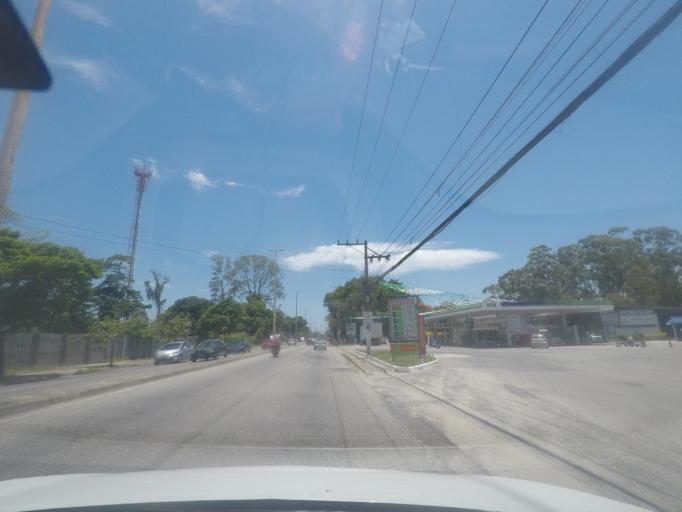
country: BR
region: Rio de Janeiro
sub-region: Itaguai
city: Itaguai
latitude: -22.9043
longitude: -43.6830
